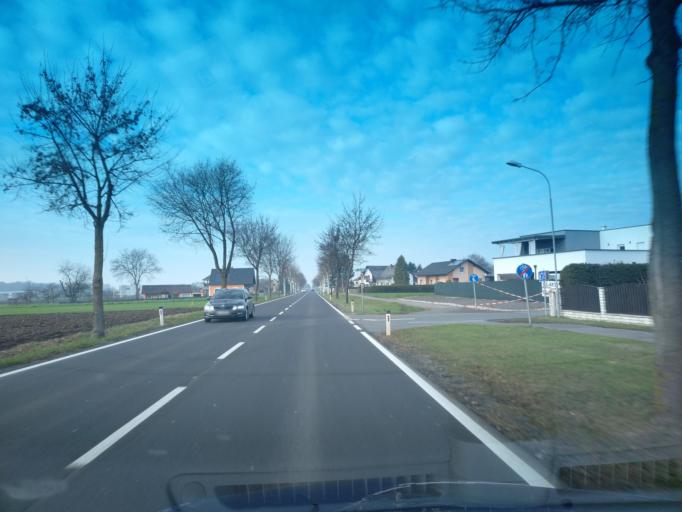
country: AT
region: Styria
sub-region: Politischer Bezirk Leibnitz
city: Sankt Veit am Vogau
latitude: 46.7358
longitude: 15.6093
